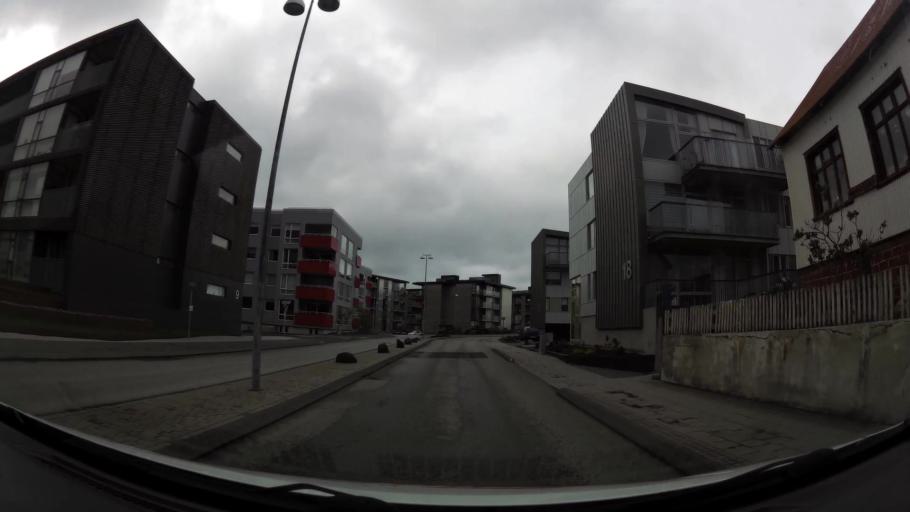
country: IS
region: Capital Region
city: Hafnarfjoerdur
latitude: 64.0699
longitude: -21.9624
